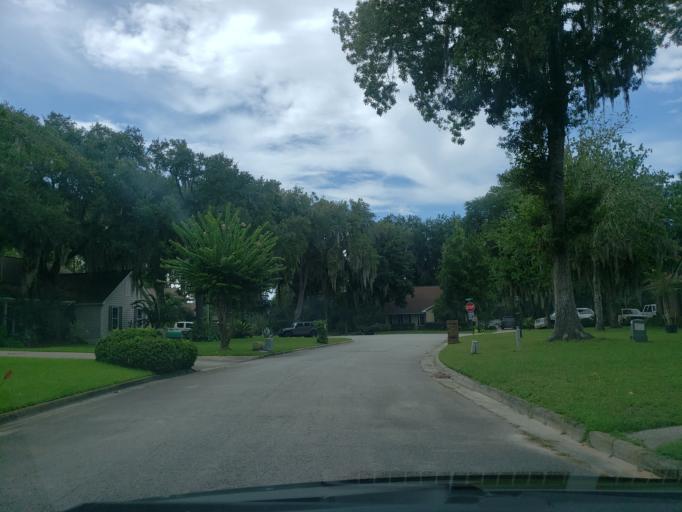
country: US
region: Georgia
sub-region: Chatham County
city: Isle of Hope
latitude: 31.9830
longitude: -81.0668
